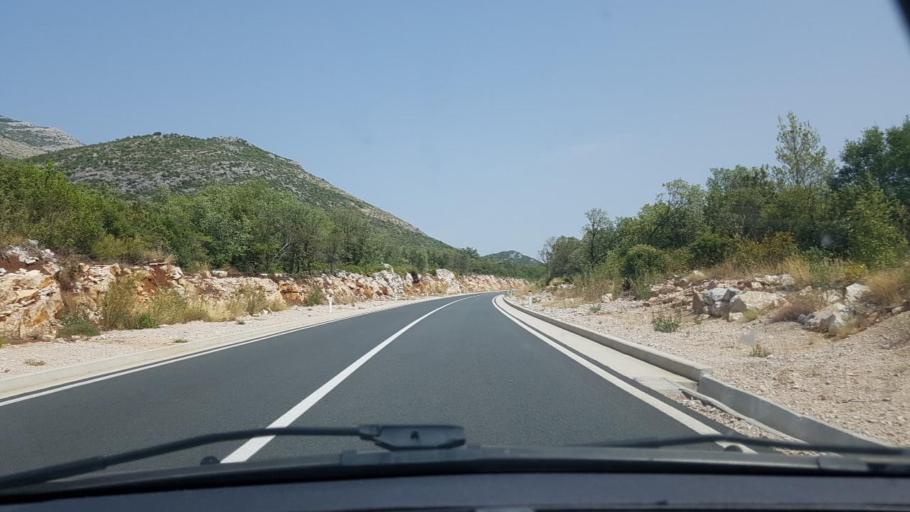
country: BA
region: Federation of Bosnia and Herzegovina
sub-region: Hercegovacko-Bosanski Kanton
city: Neum
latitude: 42.9588
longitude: 17.7192
